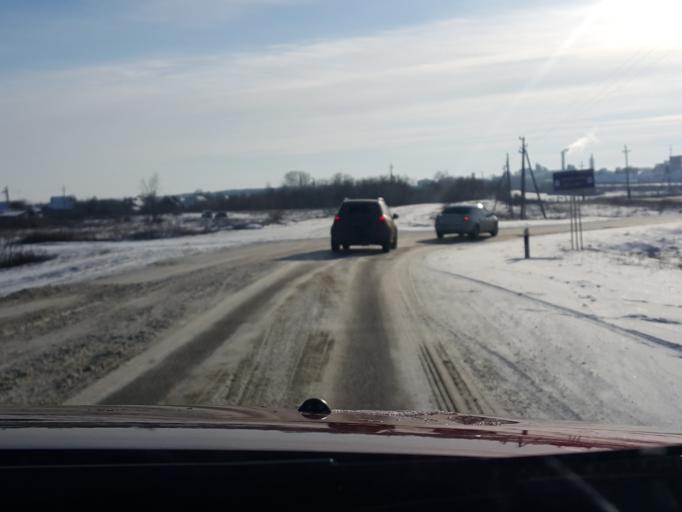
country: RU
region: Tambov
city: Znamenka
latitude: 52.4407
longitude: 41.5052
